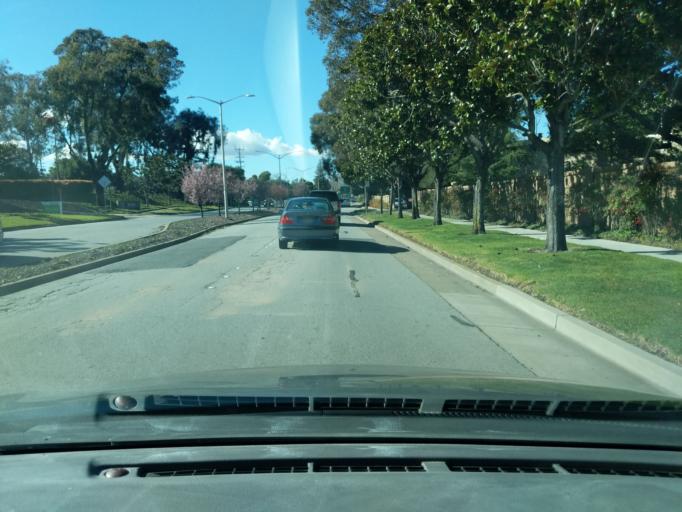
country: US
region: California
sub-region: San Mateo County
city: San Mateo
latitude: 37.5460
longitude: -122.3213
